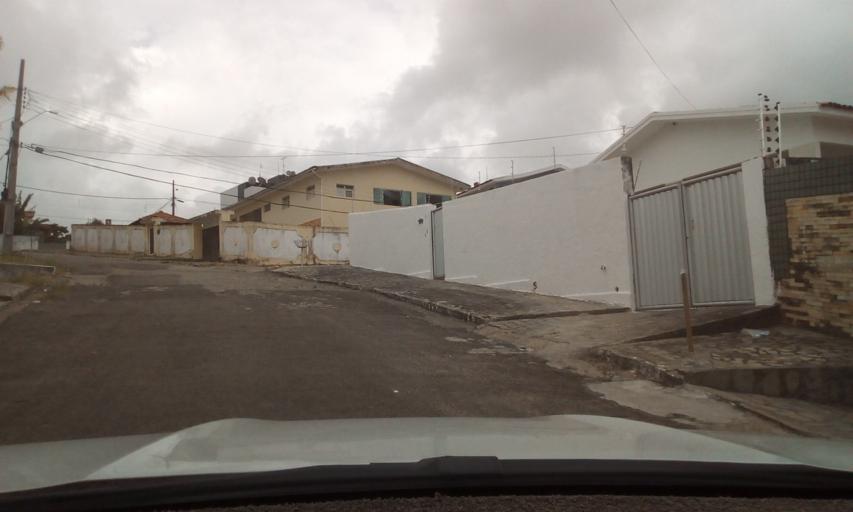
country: BR
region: Paraiba
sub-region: Joao Pessoa
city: Joao Pessoa
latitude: -7.1029
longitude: -34.8550
